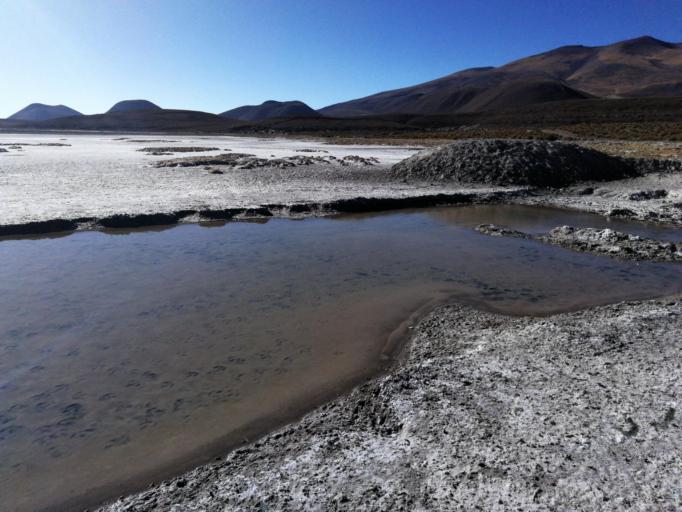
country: BO
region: Oruro
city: Cruz de Machacamarca
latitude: -19.2588
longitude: -68.3193
